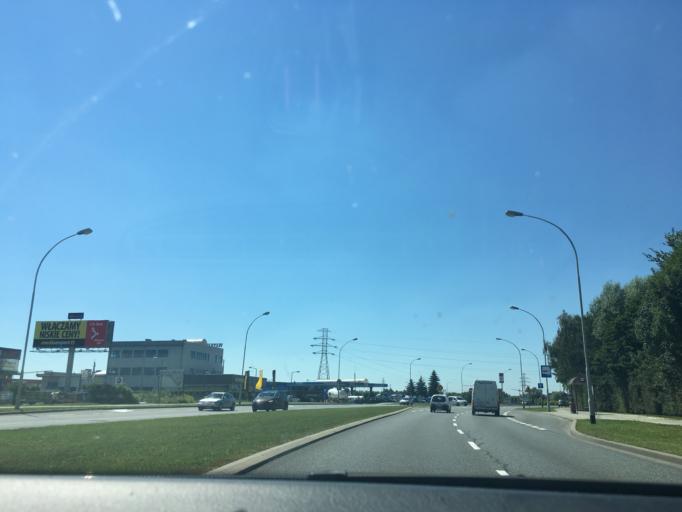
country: PL
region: Subcarpathian Voivodeship
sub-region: Rzeszow
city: Rzeszow
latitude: 50.0187
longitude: 22.0257
